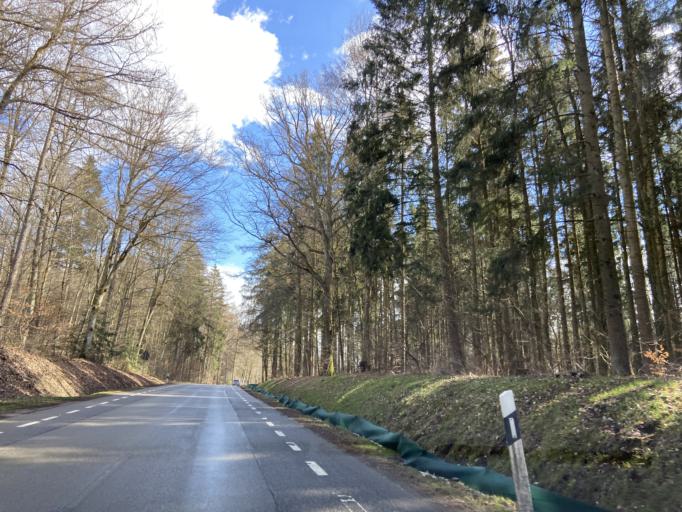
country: DE
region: Baden-Wuerttemberg
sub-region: Tuebingen Region
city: Ennetach
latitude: 48.0208
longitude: 9.3063
